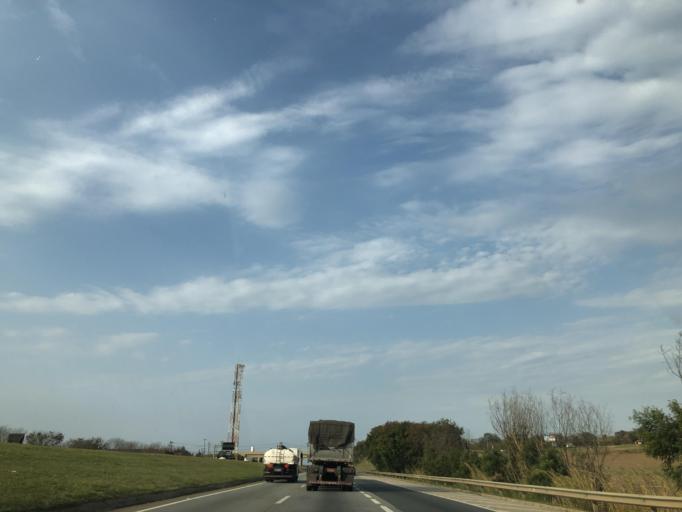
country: BR
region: Sao Paulo
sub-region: Sorocaba
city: Sorocaba
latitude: -23.4419
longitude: -47.3824
